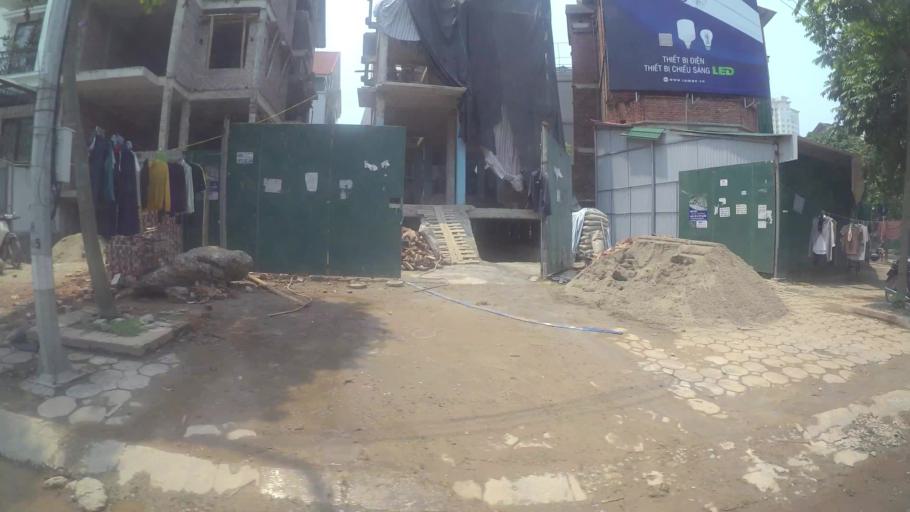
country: VN
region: Ha Noi
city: Thanh Xuan
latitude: 20.9927
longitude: 105.7799
